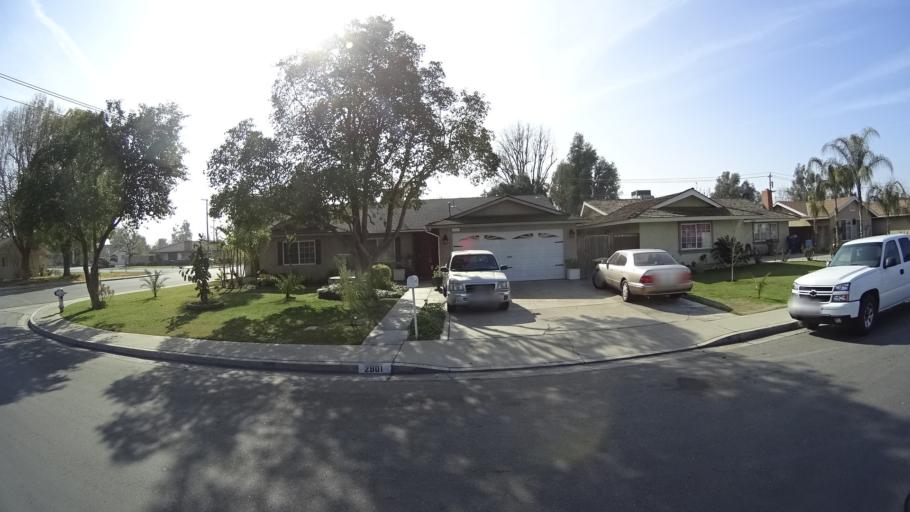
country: US
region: California
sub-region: Kern County
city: Bakersfield
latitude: 35.3235
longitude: -119.0348
